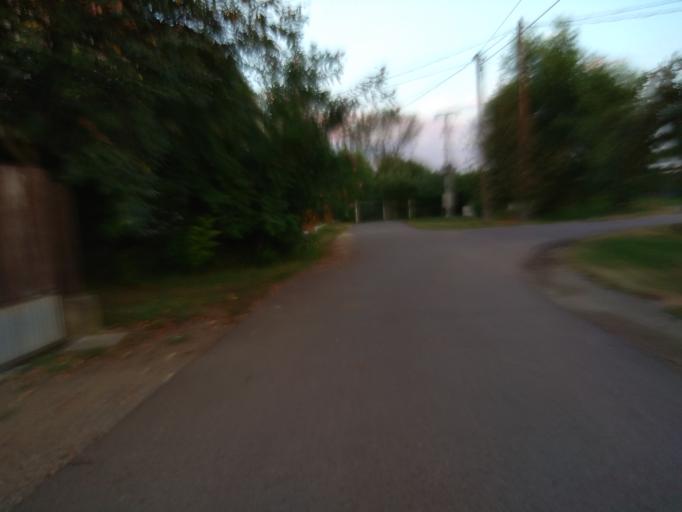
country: HU
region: Heves
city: Tarnalelesz
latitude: 48.0503
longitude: 20.1574
